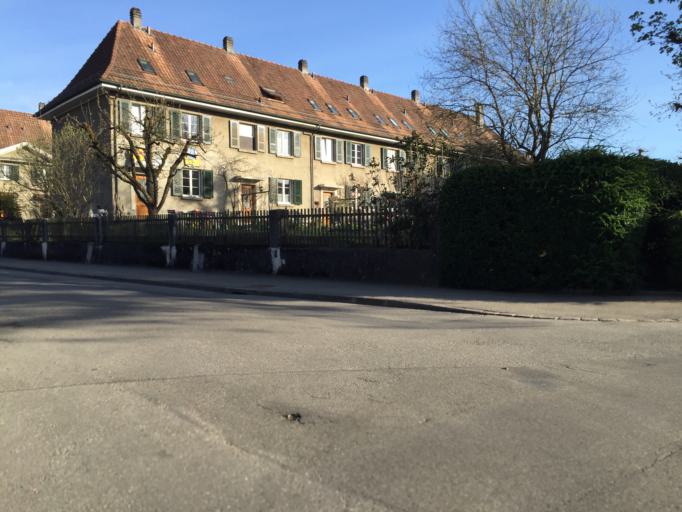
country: CH
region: Bern
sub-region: Bern-Mittelland District
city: Koniz
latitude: 46.9389
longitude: 7.4210
